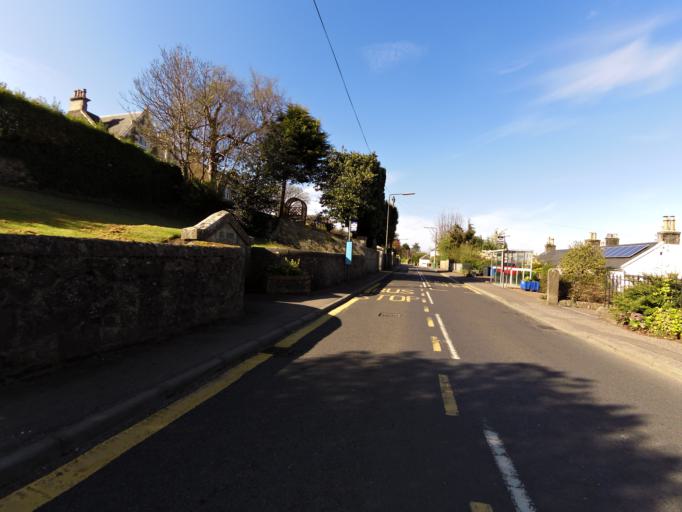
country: GB
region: Scotland
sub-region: Fife
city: Newport-On-Tay
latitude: 56.4340
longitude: -2.9519
